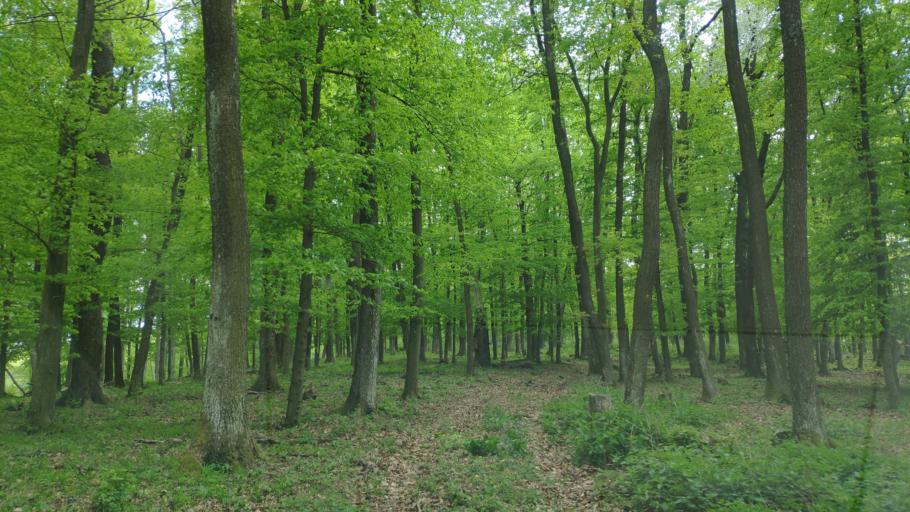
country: SK
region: Kosicky
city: Kosice
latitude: 48.6672
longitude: 21.4400
